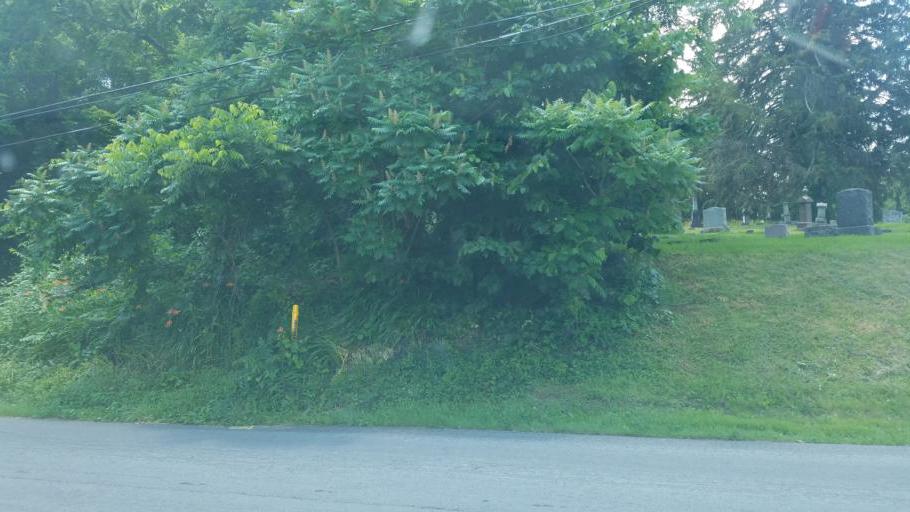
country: US
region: New York
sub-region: Wayne County
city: Clyde
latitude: 43.0759
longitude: -76.8668
